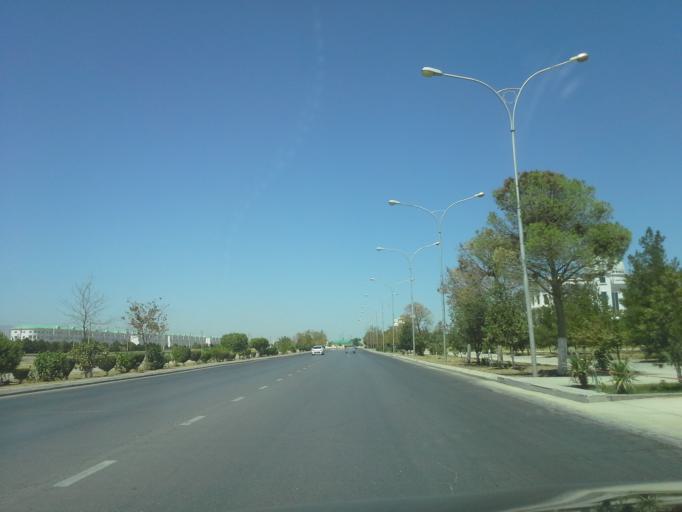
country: TM
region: Ahal
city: Ashgabat
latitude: 37.9898
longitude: 58.3246
